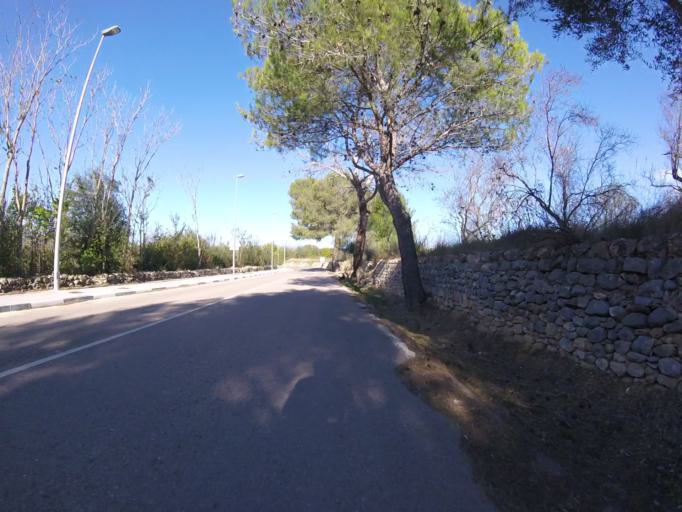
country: ES
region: Valencia
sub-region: Provincia de Castello
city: Chert/Xert
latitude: 40.4666
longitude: 0.1849
